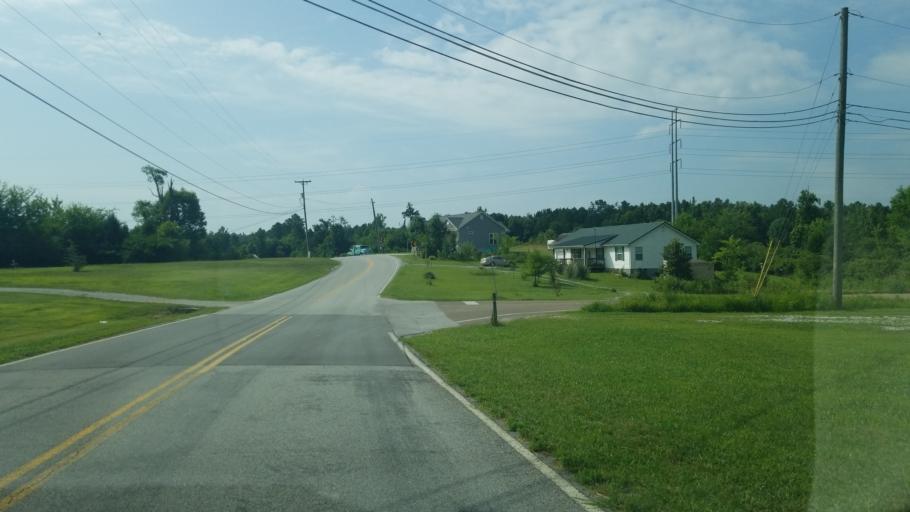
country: US
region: Tennessee
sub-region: Hamilton County
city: Apison
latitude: 35.0169
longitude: -85.0111
